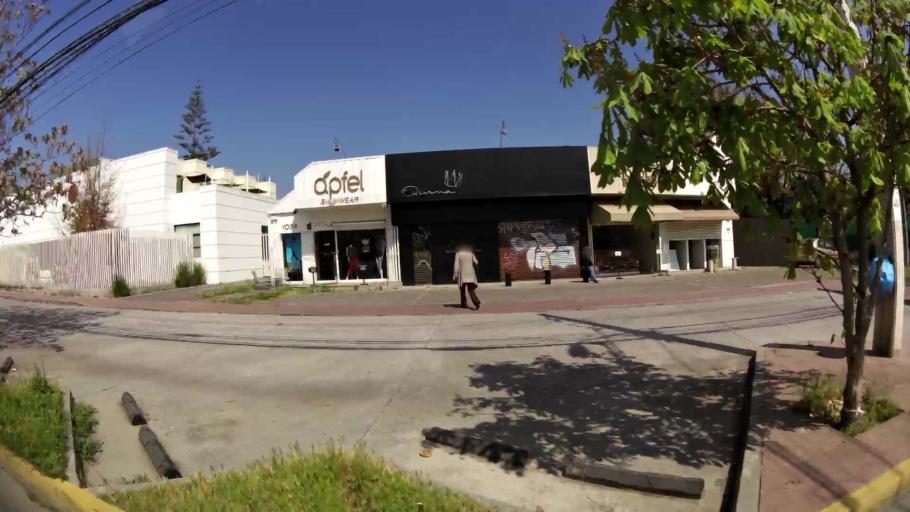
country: CL
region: Santiago Metropolitan
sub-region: Provincia de Santiago
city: Villa Presidente Frei, Nunoa, Santiago, Chile
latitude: -33.3863
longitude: -70.5774
